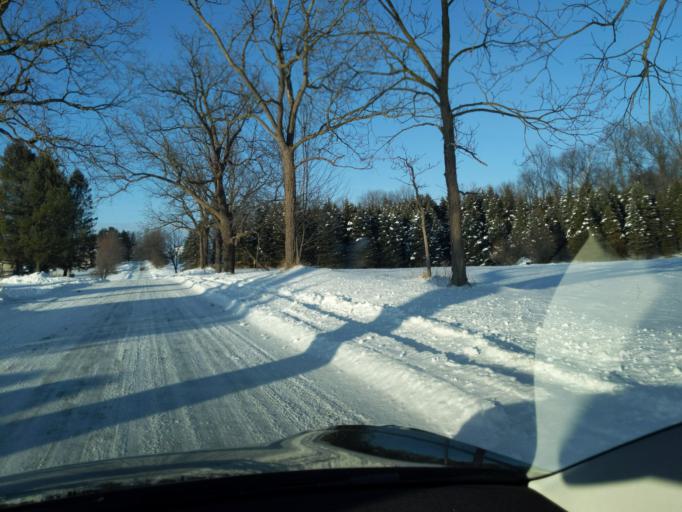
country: US
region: Michigan
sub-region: Ingham County
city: Stockbridge
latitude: 42.4701
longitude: -84.1194
